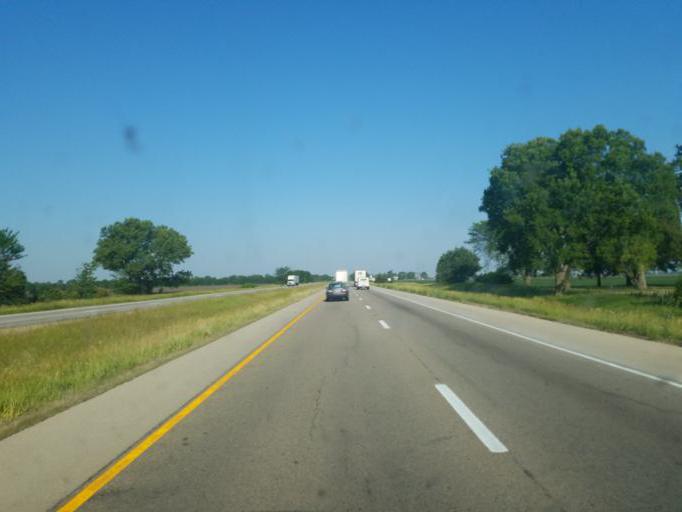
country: US
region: Illinois
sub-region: Grundy County
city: Morris
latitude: 41.3779
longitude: -88.5033
